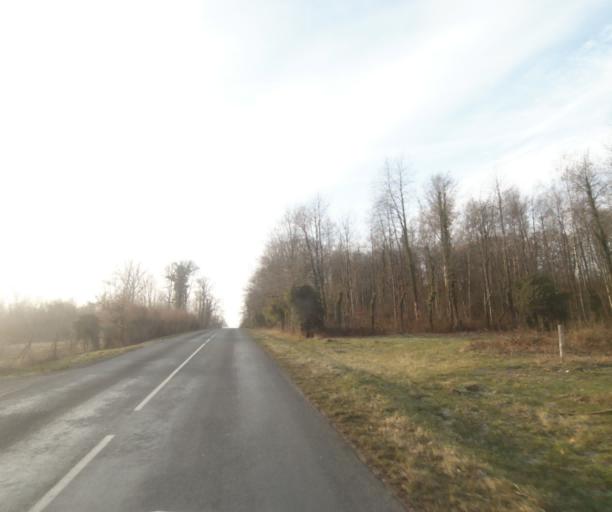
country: FR
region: Champagne-Ardenne
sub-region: Departement de la Haute-Marne
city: Chancenay
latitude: 48.6921
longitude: 4.9456
